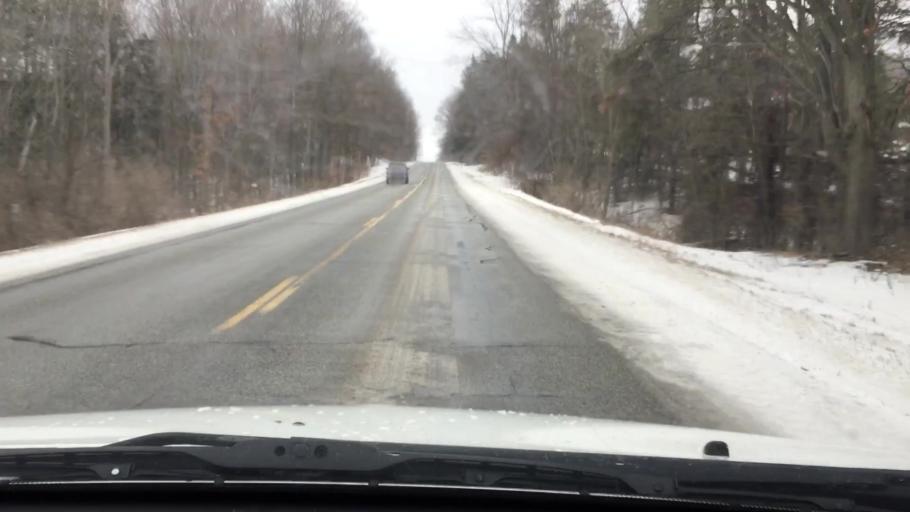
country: US
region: Michigan
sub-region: Wexford County
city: Cadillac
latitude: 44.1858
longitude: -85.4056
